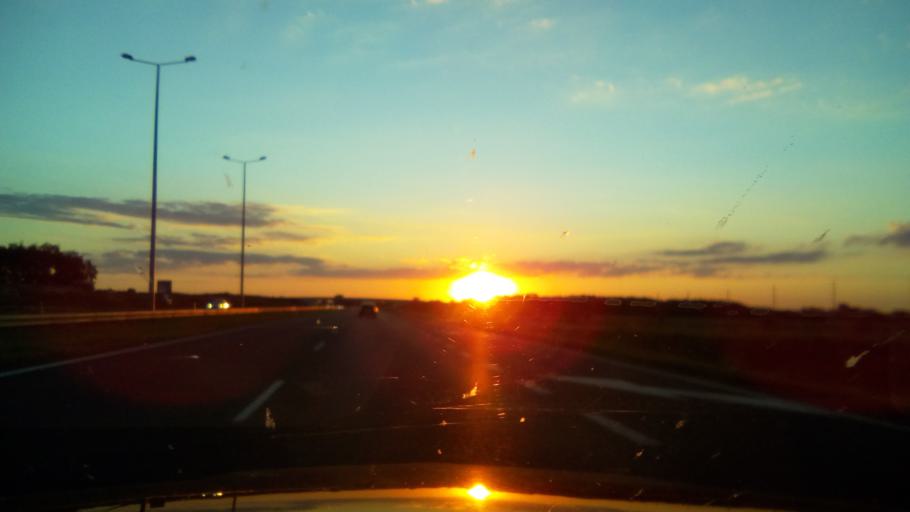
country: PL
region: Lodz Voivodeship
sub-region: Powiat zgierski
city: Parzeczew
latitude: 51.9463
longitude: 19.1731
